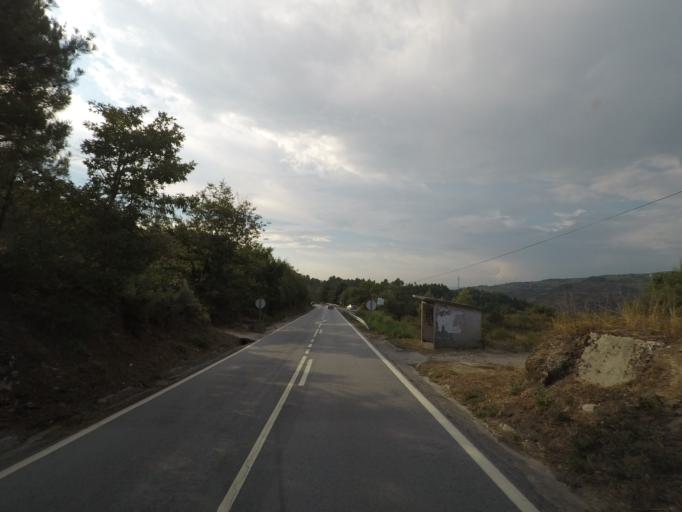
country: PT
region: Porto
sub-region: Baiao
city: Valadares
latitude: 41.2080
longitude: -7.9746
